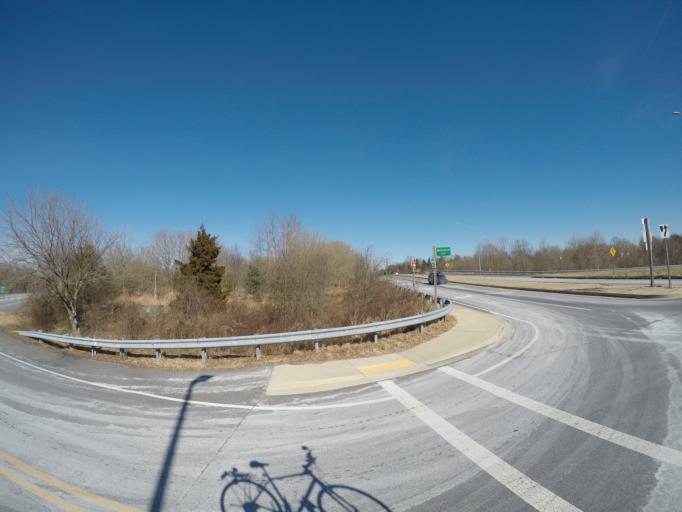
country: US
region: Maryland
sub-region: Howard County
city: Columbia
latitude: 39.2466
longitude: -76.8187
